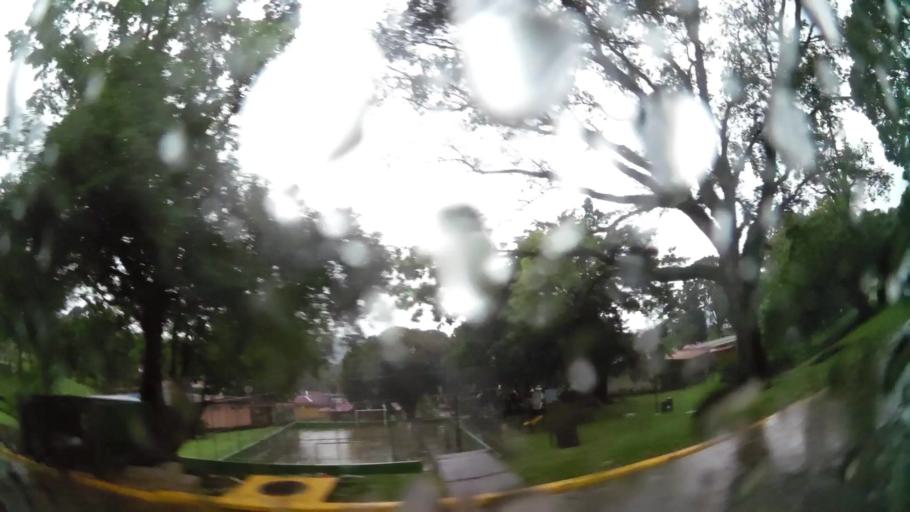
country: PA
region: Panama
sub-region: Distrito de Panama
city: Paraiso
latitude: 9.0340
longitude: -79.6278
